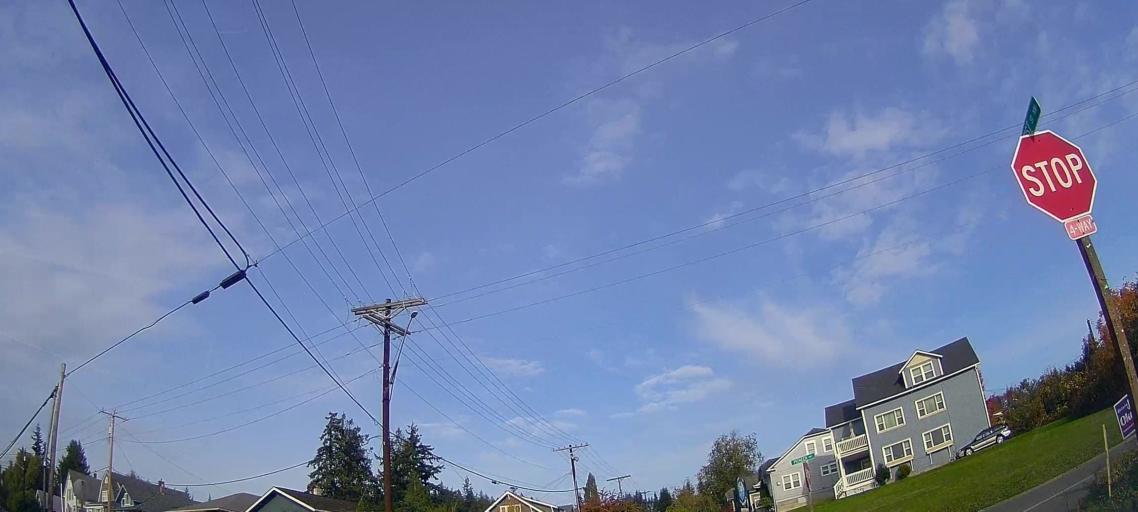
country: US
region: Washington
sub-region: Snohomish County
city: Stanwood
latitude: 48.2437
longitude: -122.3475
